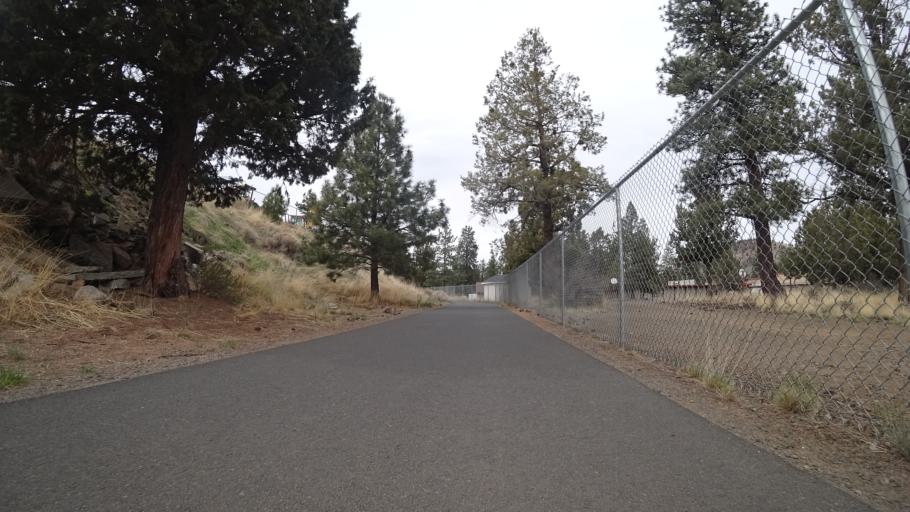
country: US
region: Oregon
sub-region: Deschutes County
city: Bend
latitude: 44.0496
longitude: -121.2876
